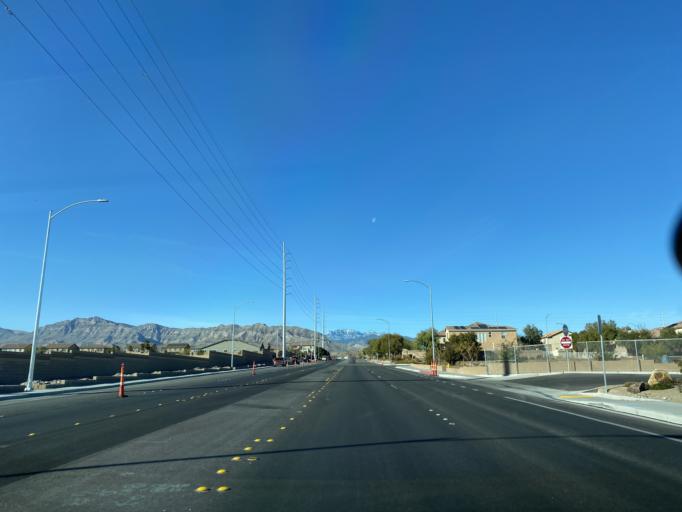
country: US
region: Nevada
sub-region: Clark County
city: Summerlin South
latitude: 36.2994
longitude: -115.3104
